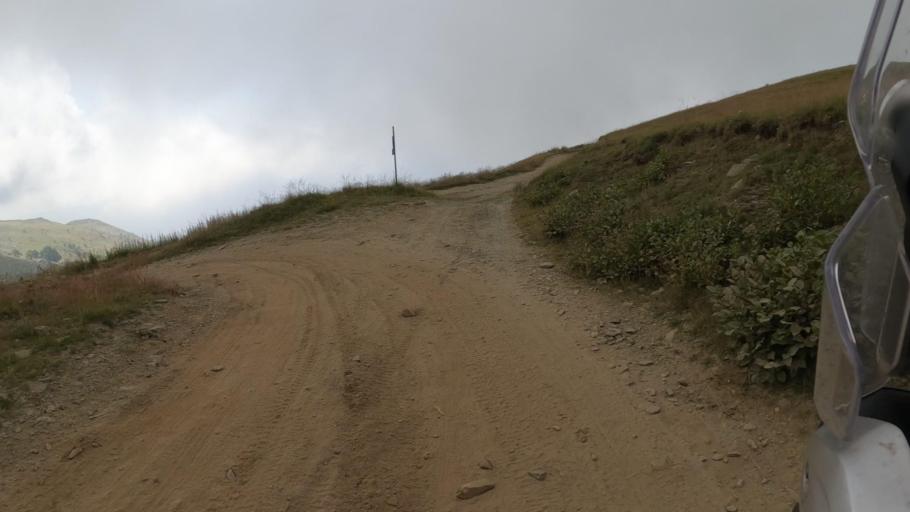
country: IT
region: Piedmont
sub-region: Provincia di Torino
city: Lemie
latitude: 45.1710
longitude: 7.2781
